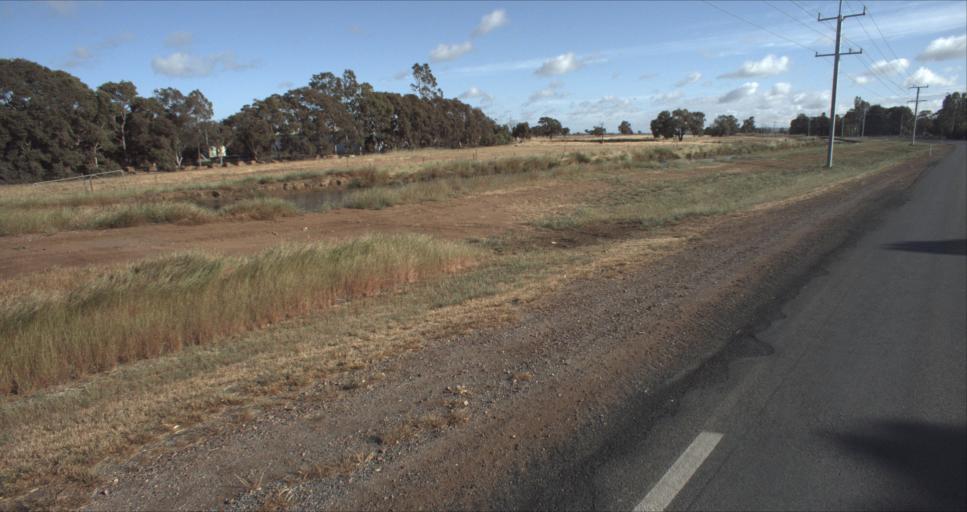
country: AU
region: New South Wales
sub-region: Leeton
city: Leeton
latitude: -34.5383
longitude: 146.3875
